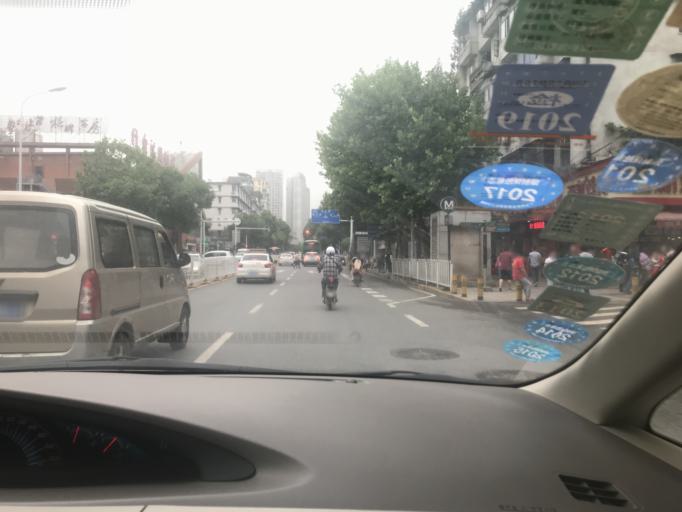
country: CN
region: Hubei
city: Wuhan
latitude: 30.5523
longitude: 114.2629
